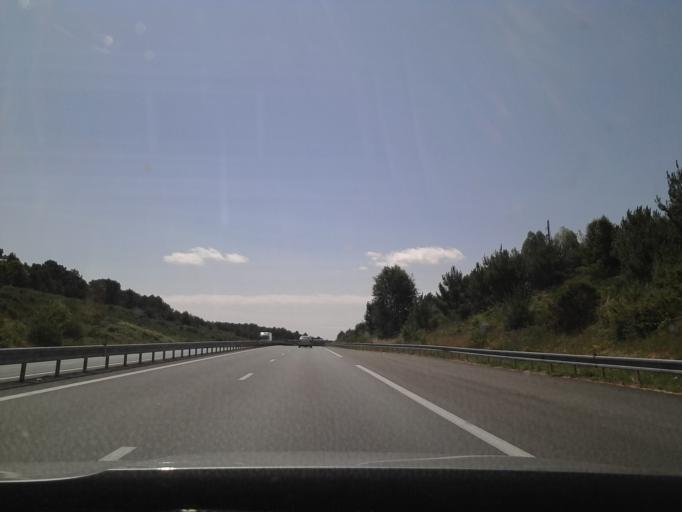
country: FR
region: Pays de la Loire
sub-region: Departement de la Sarthe
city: Ecommoy
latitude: 47.8477
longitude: 0.3013
